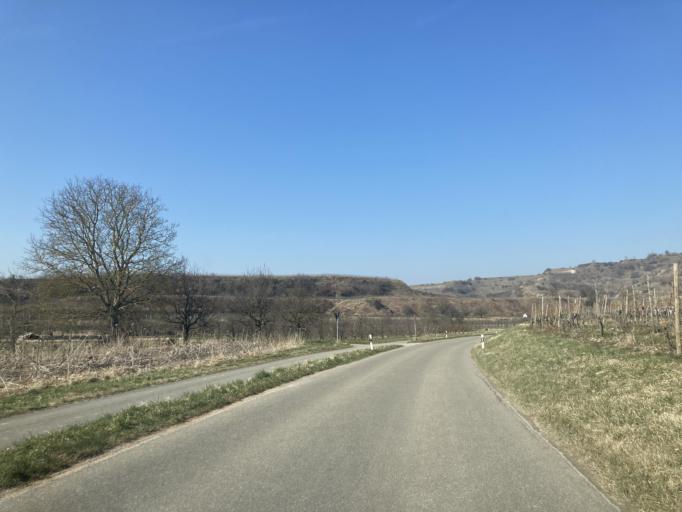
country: DE
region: Baden-Wuerttemberg
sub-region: Freiburg Region
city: Vogtsburg
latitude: 48.0829
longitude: 7.6391
